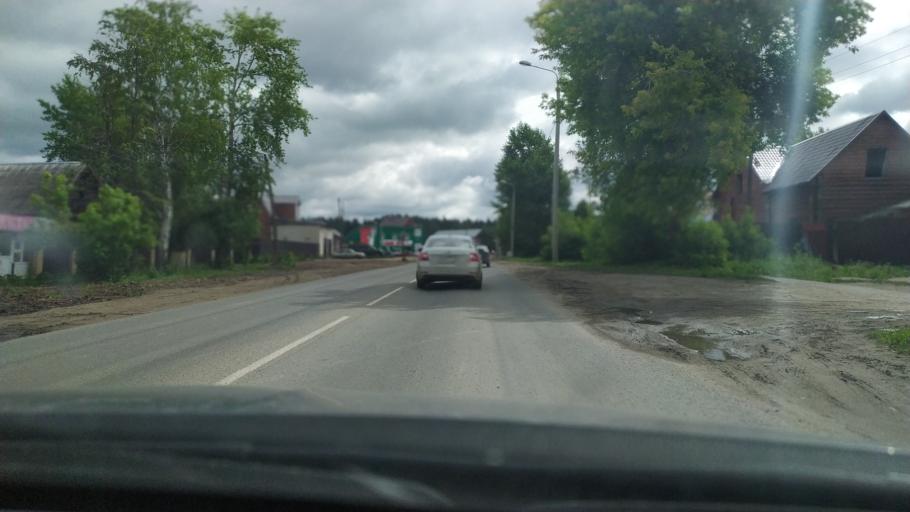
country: RU
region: Perm
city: Froly
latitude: 57.9772
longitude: 56.3103
